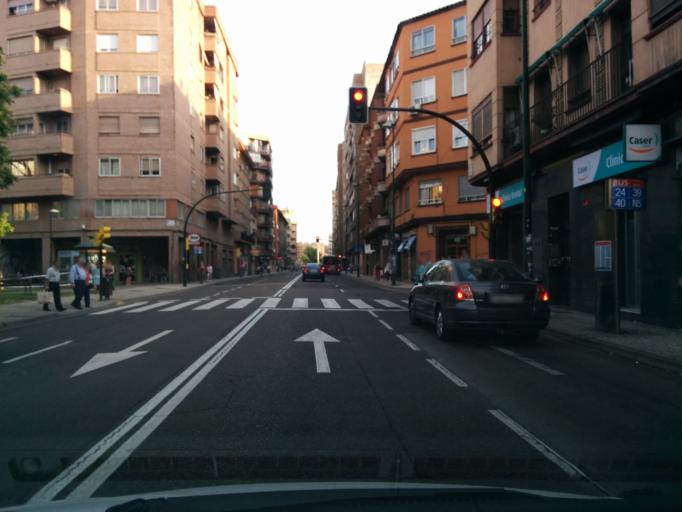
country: ES
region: Aragon
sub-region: Provincia de Zaragoza
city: Zaragoza
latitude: 41.6435
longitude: -0.8729
